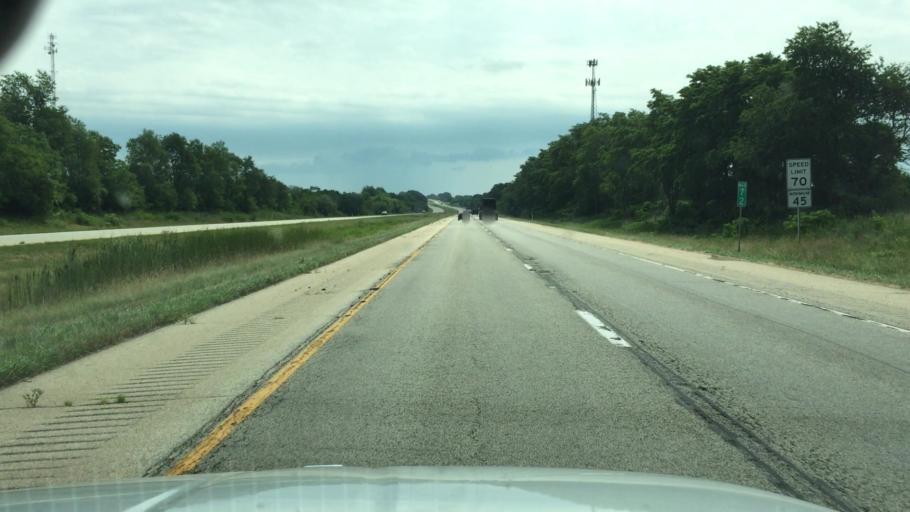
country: US
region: Illinois
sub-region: Peoria County
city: Elmwood
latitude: 40.8455
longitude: -89.9143
